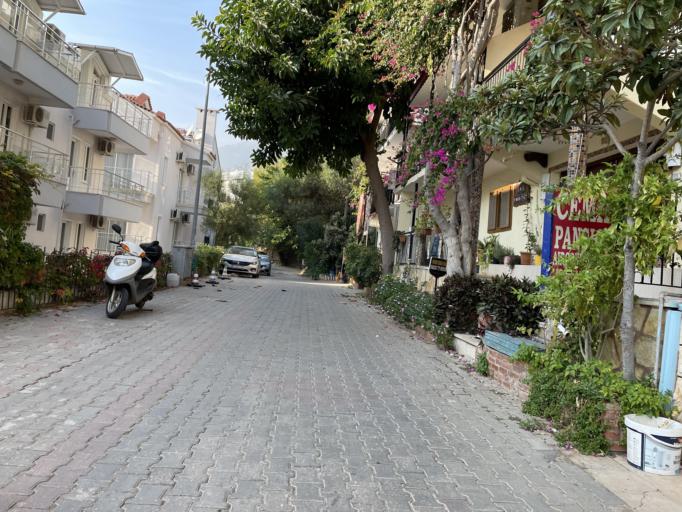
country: TR
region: Antalya
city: Kas
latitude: 36.1982
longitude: 29.6445
